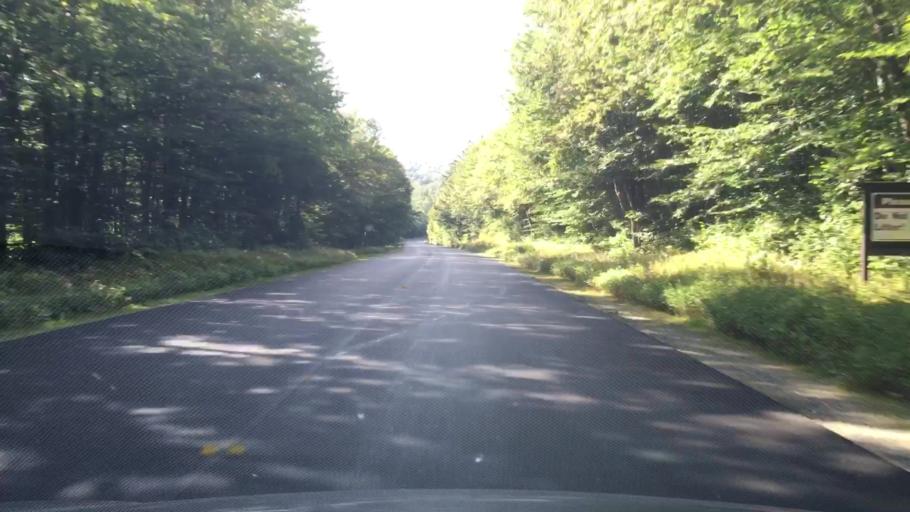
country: US
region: New Hampshire
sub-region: Carroll County
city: Tamworth
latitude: 44.0037
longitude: -71.4176
